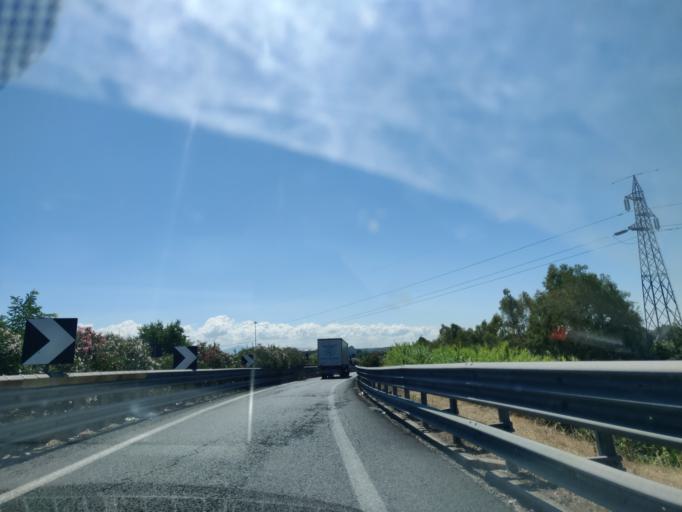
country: IT
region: Latium
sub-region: Citta metropolitana di Roma Capitale
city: Vitinia
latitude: 41.8175
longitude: 12.3887
